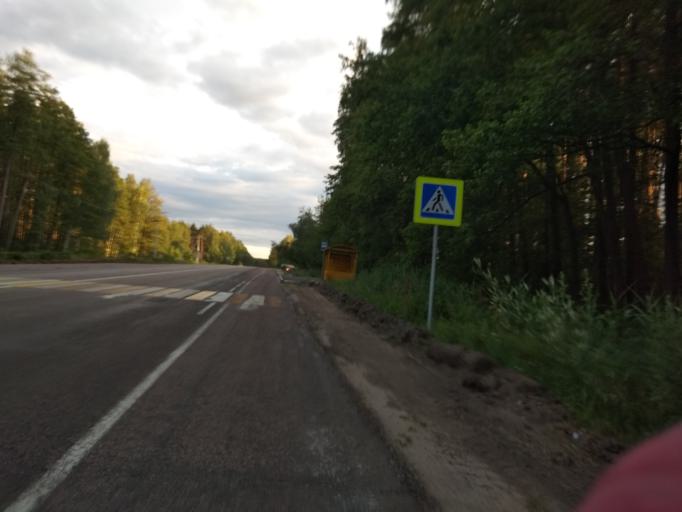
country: RU
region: Moskovskaya
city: Misheronskiy
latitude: 55.6346
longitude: 39.7469
